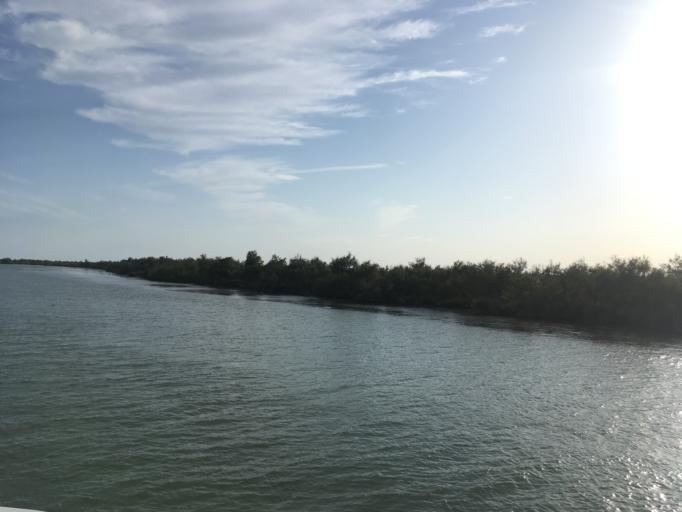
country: FR
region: Provence-Alpes-Cote d'Azur
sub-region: Departement des Bouches-du-Rhone
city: Saintes-Maries-de-la-Mer
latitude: 43.4654
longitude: 4.3930
